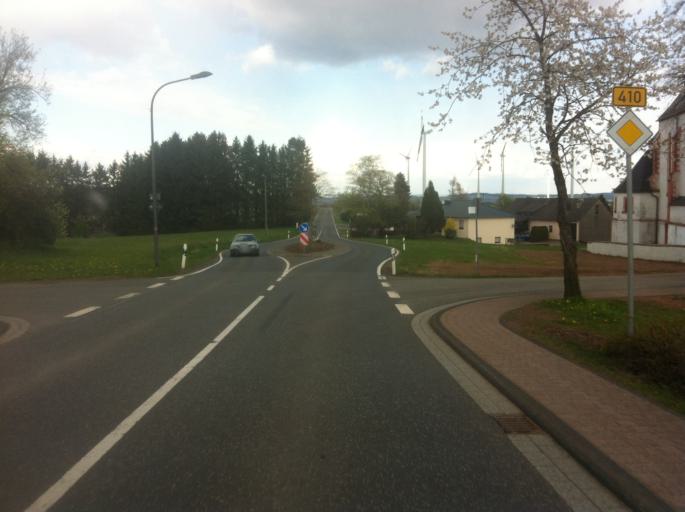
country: DE
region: Rheinland-Pfalz
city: Lichtenborn
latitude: 50.1106
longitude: 6.2939
